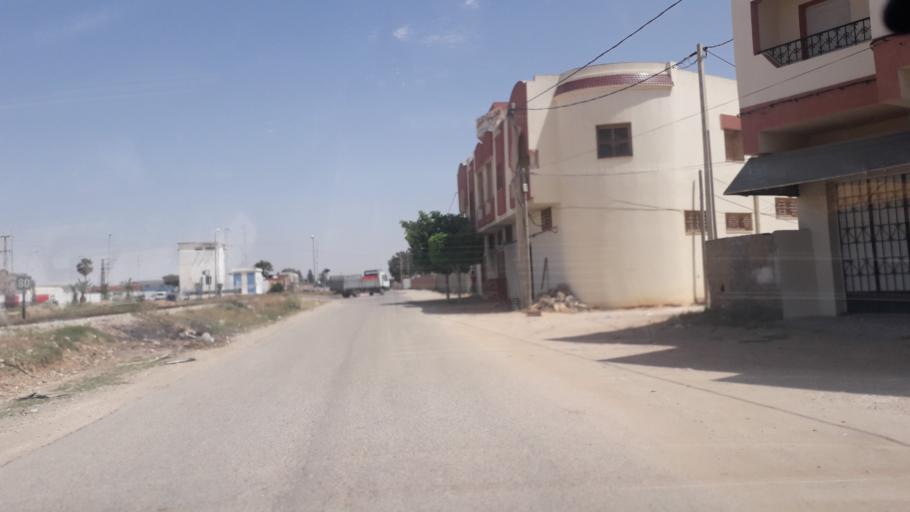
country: TN
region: Safaqis
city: Al Qarmadah
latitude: 34.8338
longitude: 10.7653
